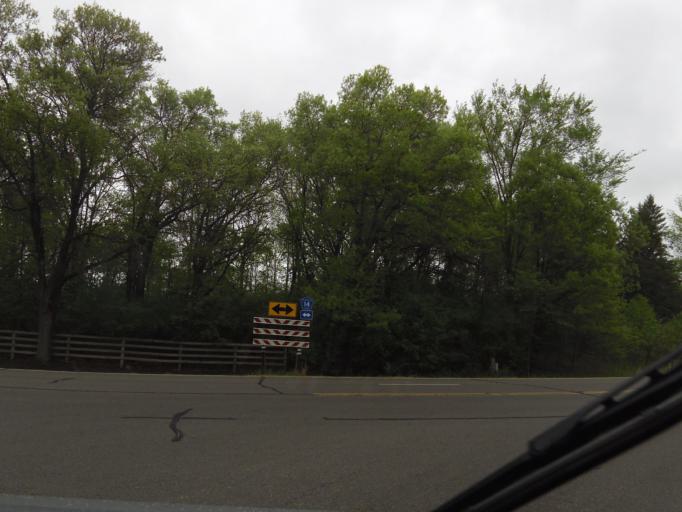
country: US
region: Minnesota
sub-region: Washington County
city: Oak Park Heights
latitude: 45.0073
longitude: -92.8225
